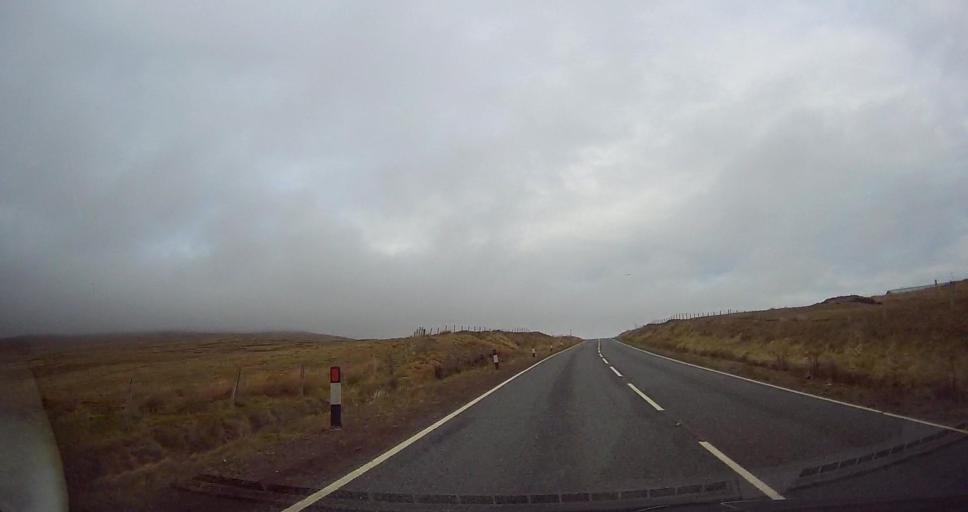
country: GB
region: Scotland
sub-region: Shetland Islands
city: Sandwick
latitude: 60.0062
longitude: -1.2760
